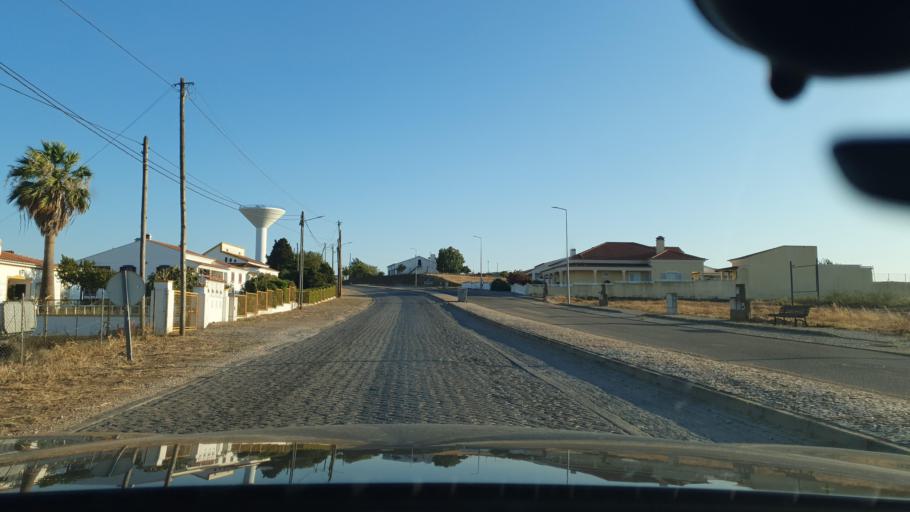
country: PT
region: Portalegre
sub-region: Fronteira
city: Fronteira
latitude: 38.9463
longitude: -7.6766
